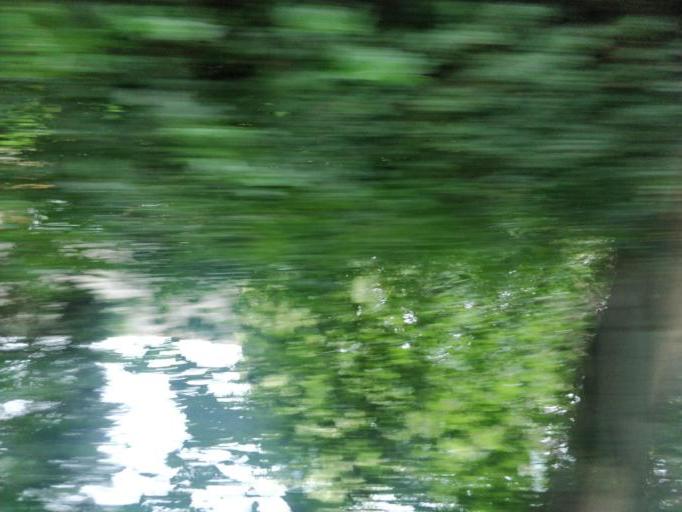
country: GB
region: England
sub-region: Lancashire
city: Ormskirk
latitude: 53.6096
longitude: -2.9160
